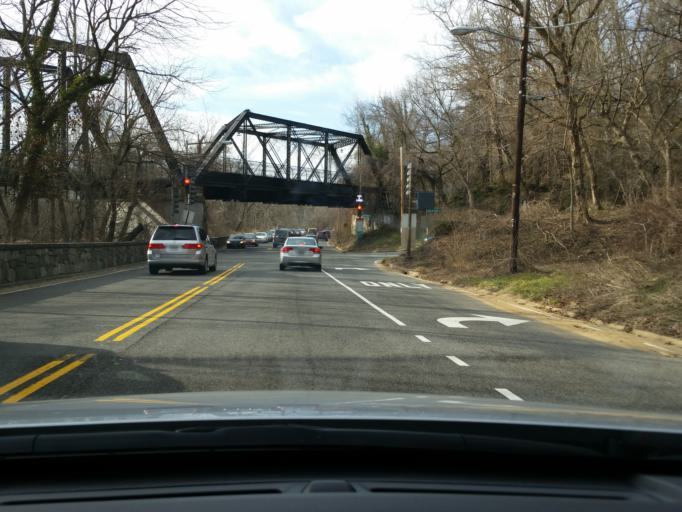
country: US
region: Maryland
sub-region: Montgomery County
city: Brookmont
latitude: 38.9245
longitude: -77.1067
